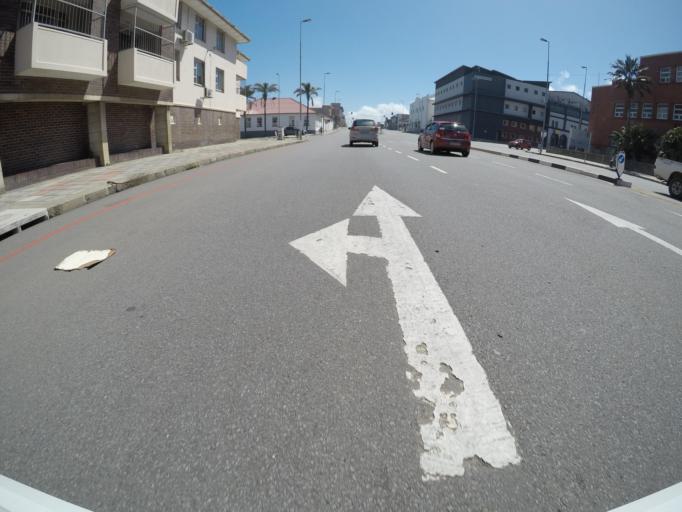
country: ZA
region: Eastern Cape
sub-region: Buffalo City Metropolitan Municipality
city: East London
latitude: -33.0189
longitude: 27.9085
